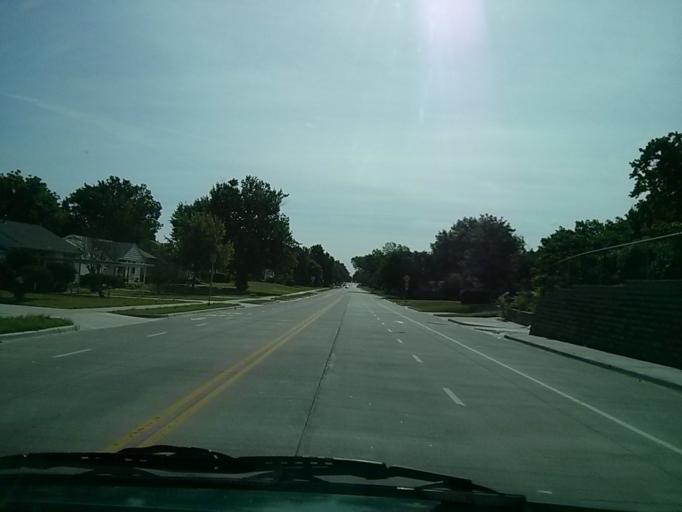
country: US
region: Oklahoma
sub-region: Tulsa County
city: Tulsa
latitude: 36.1551
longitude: -95.9127
